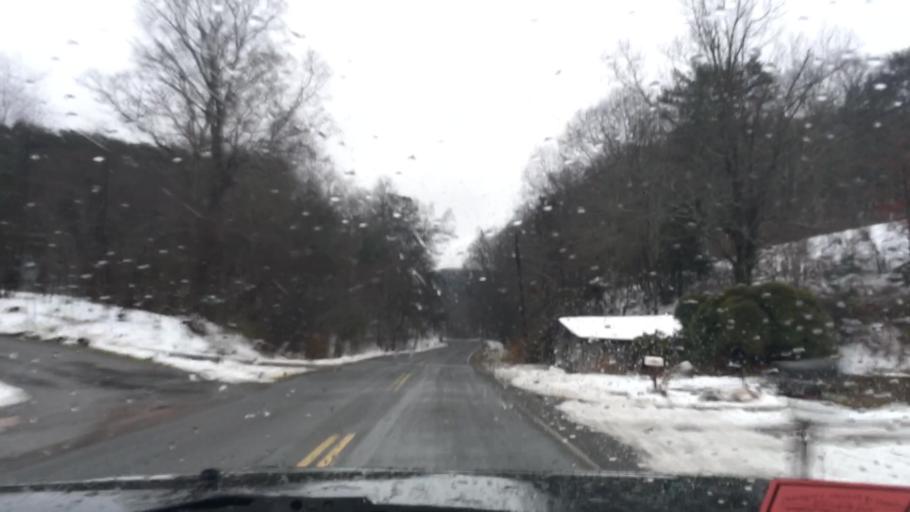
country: US
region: Virginia
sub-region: Pulaski County
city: Pulaski
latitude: 37.0194
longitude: -80.7085
